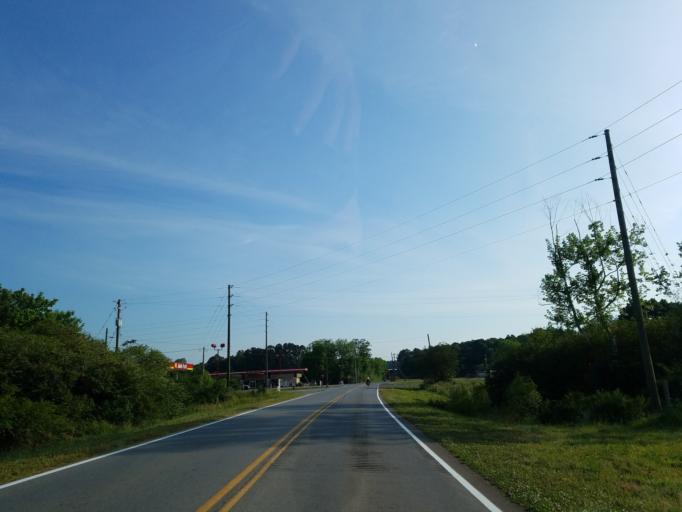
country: US
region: Georgia
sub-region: Chattooga County
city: Summerville
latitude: 34.4667
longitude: -85.2683
